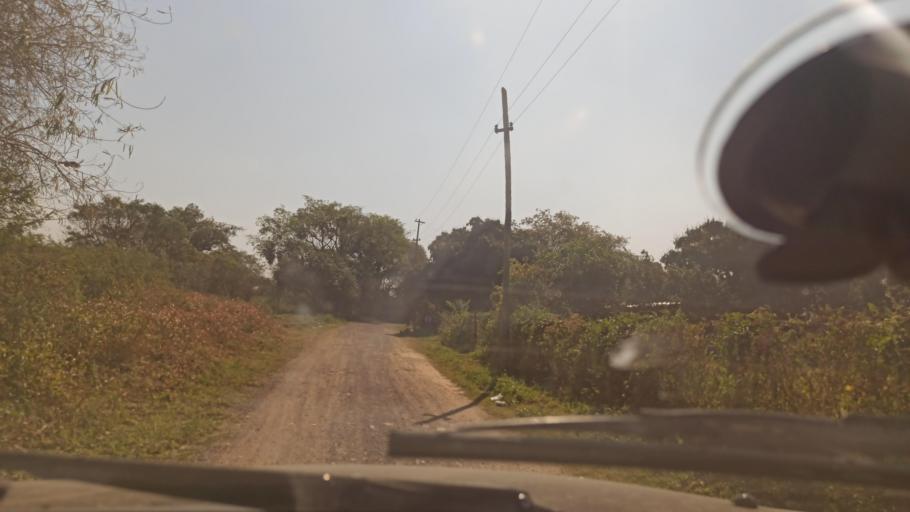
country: AR
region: Formosa
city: Clorinda
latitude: -25.3242
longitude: -57.6921
